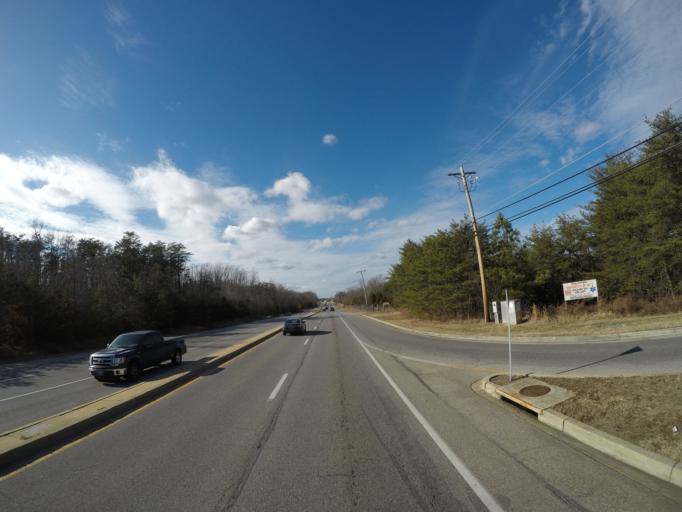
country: US
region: Maryland
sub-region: Charles County
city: Saint Charles
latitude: 38.6053
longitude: -76.9509
